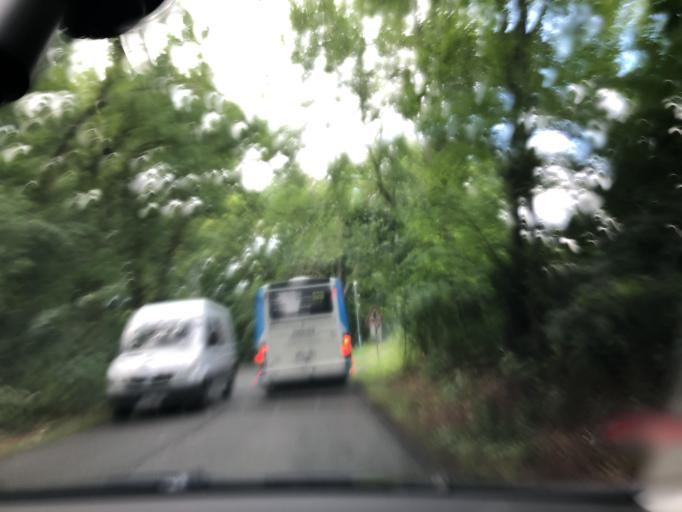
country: CZ
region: Central Bohemia
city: Nelahozeves
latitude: 50.2564
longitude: 14.2988
